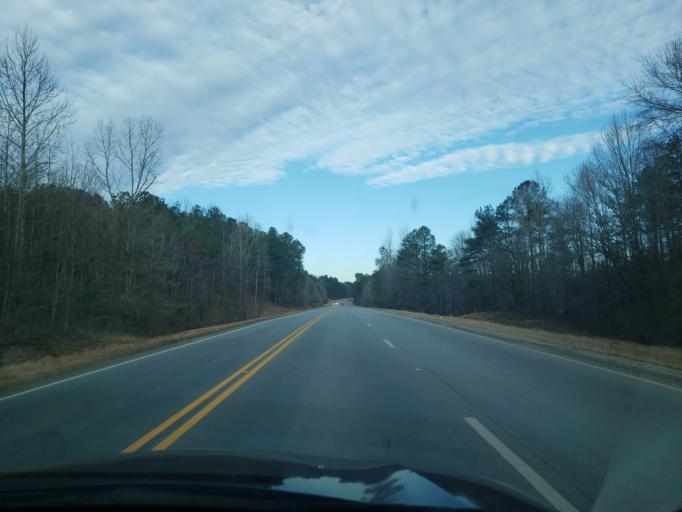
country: US
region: Alabama
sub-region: Randolph County
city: Wedowee
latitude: 33.4083
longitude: -85.5380
